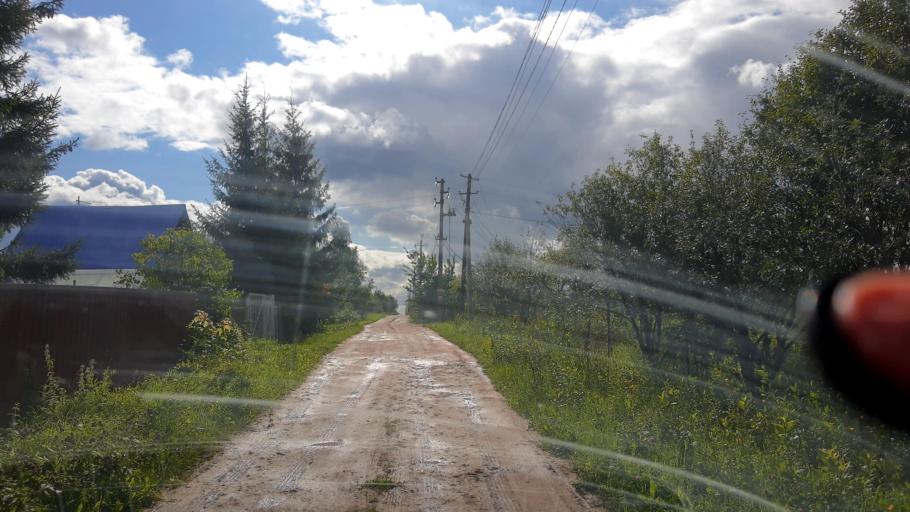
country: RU
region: Bashkortostan
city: Iglino
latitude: 54.7680
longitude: 56.4582
